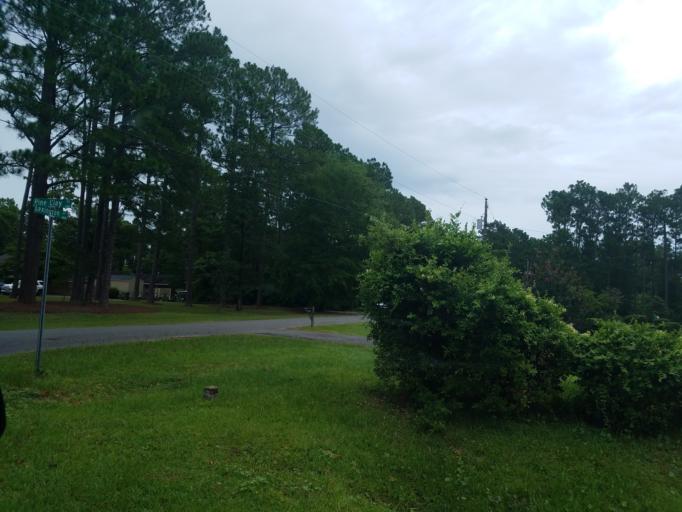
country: US
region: North Carolina
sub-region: New Hanover County
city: Kings Grant
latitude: 34.2408
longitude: -77.8608
